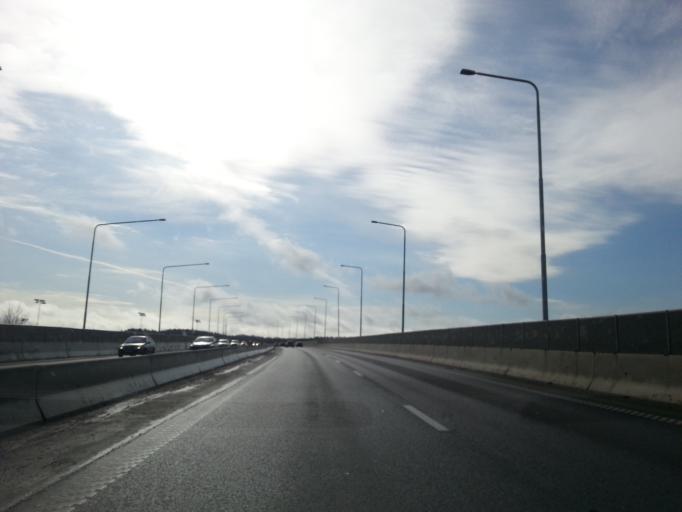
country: SE
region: Vaestra Goetaland
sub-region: Kungalvs Kommun
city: Kungalv
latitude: 57.8683
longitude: 11.9694
